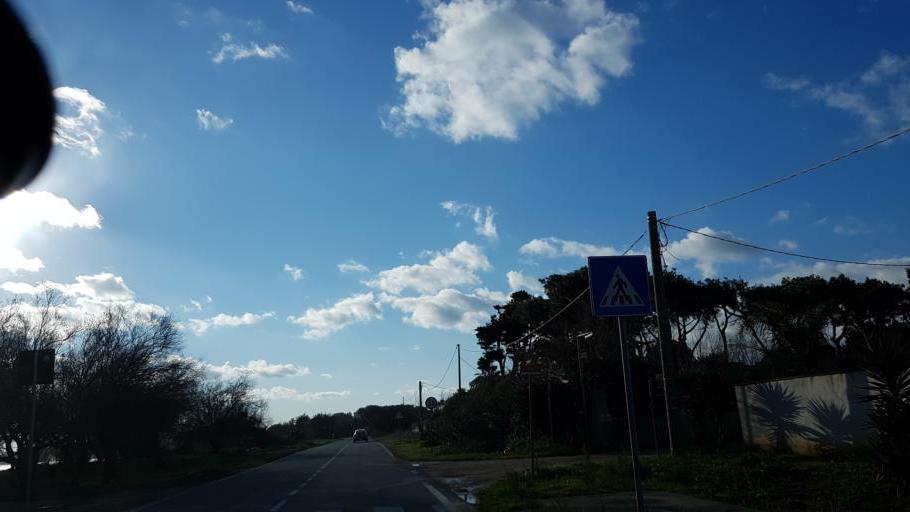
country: IT
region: Apulia
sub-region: Provincia di Brindisi
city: Materdomini
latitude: 40.6719
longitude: 17.9458
